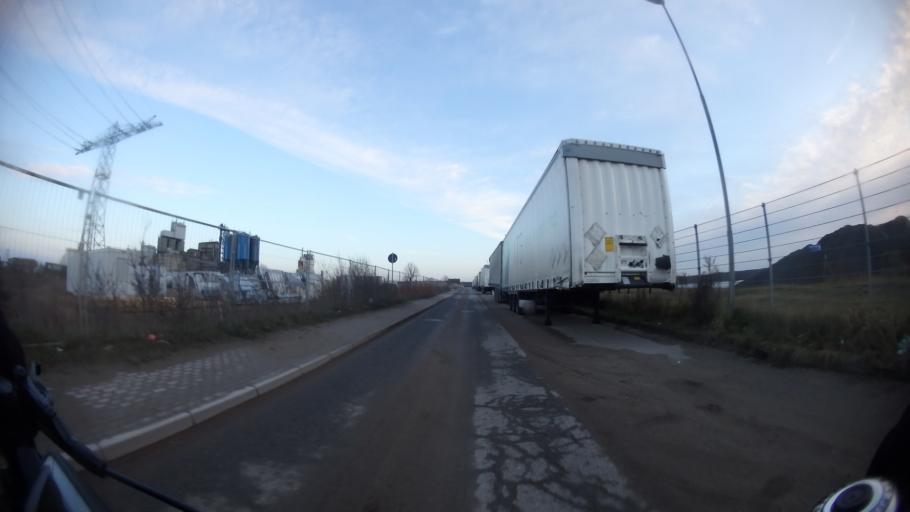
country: DE
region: Mecklenburg-Vorpommern
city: Selmsdorf
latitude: 53.8984
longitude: 10.8057
